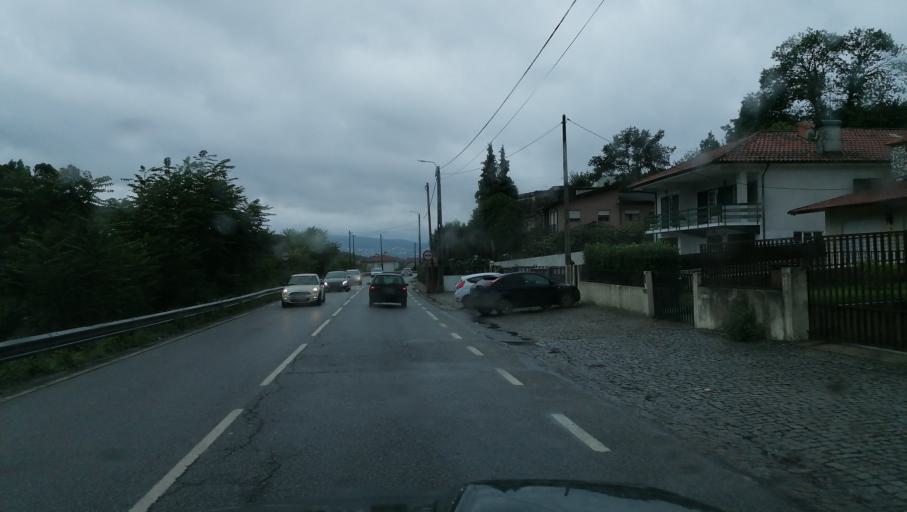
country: PT
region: Braga
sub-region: Guimaraes
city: Moreira de Conegos
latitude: 41.3969
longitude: -8.3258
